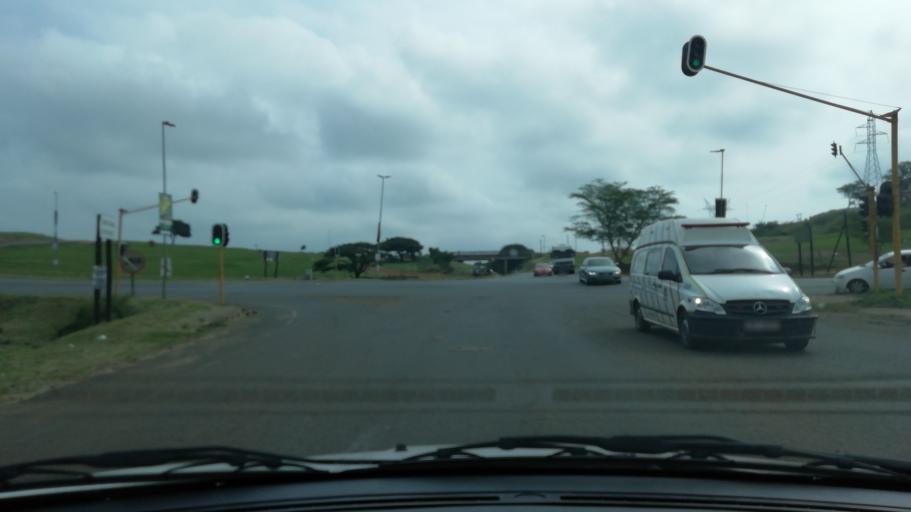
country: ZA
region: KwaZulu-Natal
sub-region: uThungulu District Municipality
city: Empangeni
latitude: -28.7415
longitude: 31.8825
